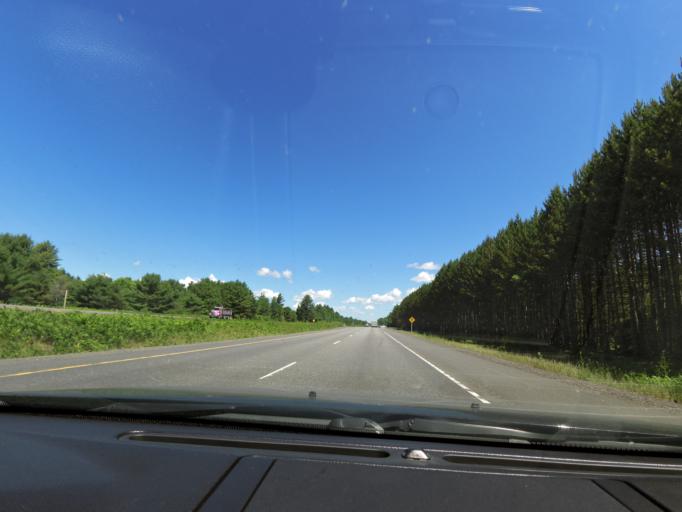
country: CA
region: Ontario
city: Bracebridge
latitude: 45.1243
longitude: -79.3107
